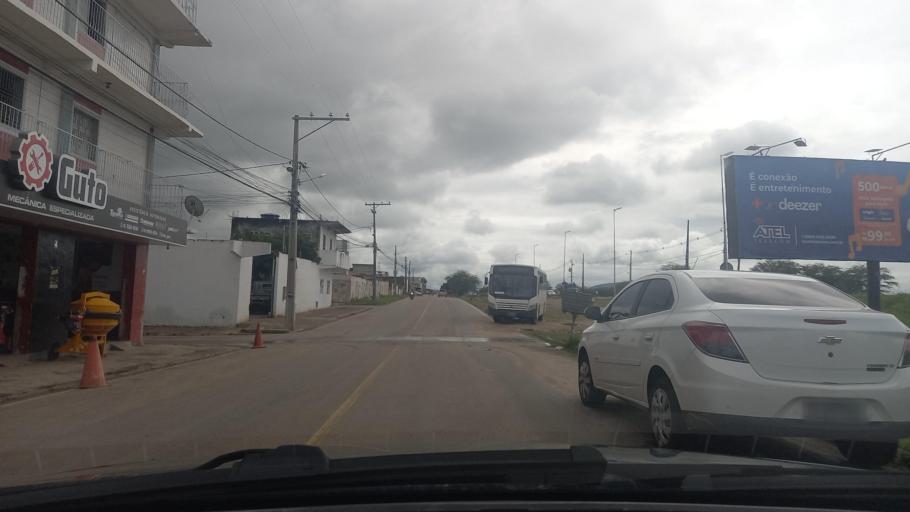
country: BR
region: Bahia
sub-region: Paulo Afonso
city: Paulo Afonso
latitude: -9.4003
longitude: -38.2401
